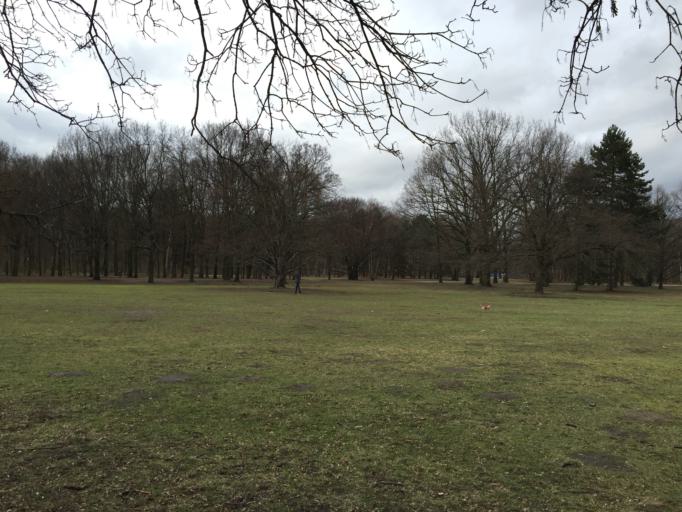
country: DE
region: Berlin
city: Tiergarten Bezirk
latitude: 52.5131
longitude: 13.3747
